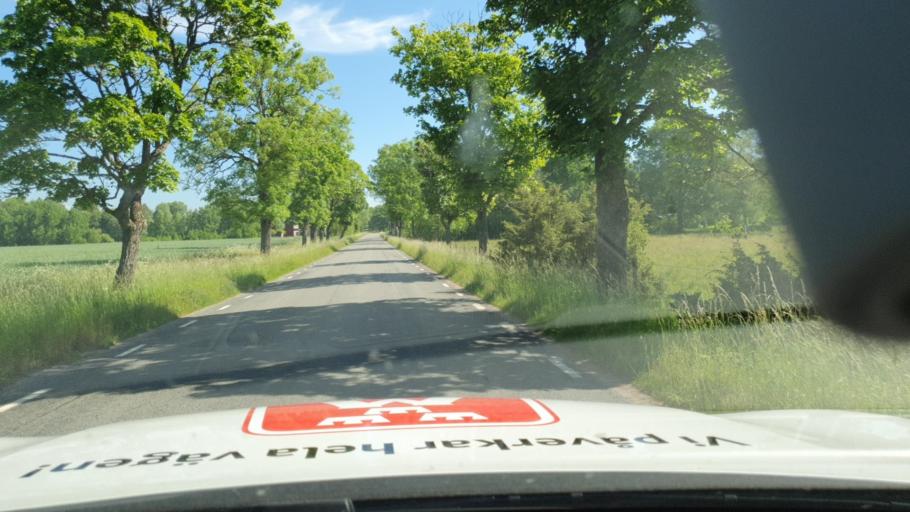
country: SE
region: Vaestra Goetaland
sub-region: Tidaholms Kommun
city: Olofstorp
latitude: 58.2749
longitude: 13.9184
